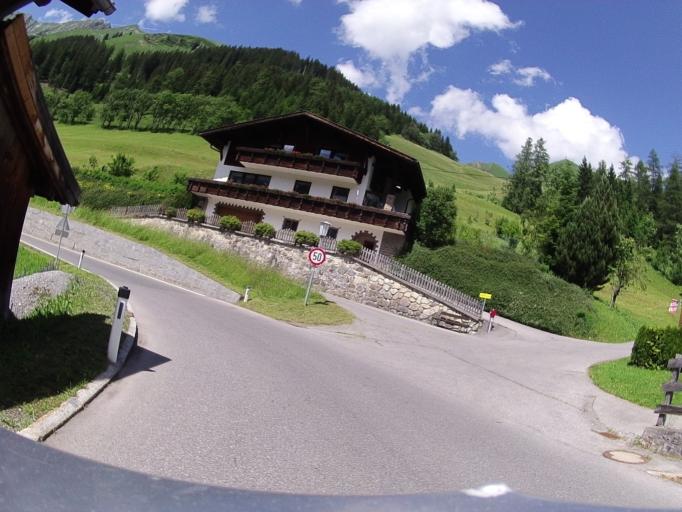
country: AT
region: Tyrol
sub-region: Politischer Bezirk Reutte
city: Elmen
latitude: 47.3093
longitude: 10.5845
